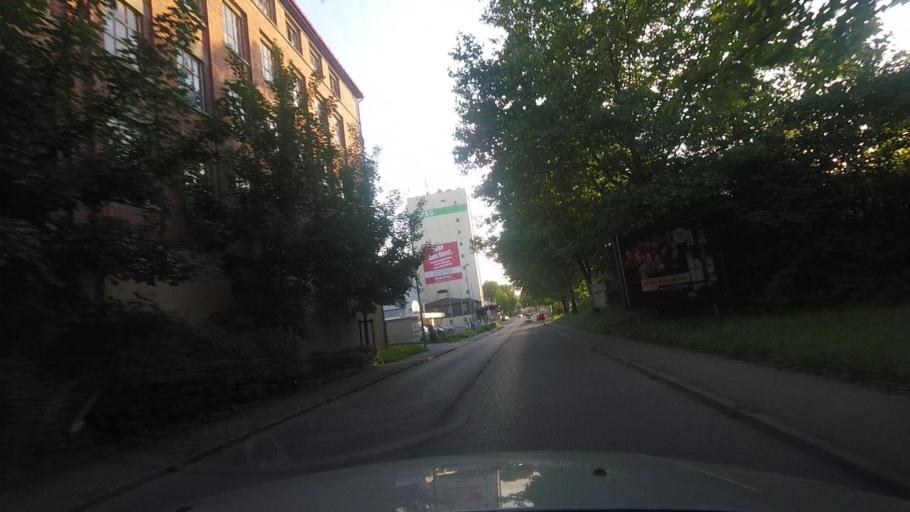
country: DE
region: Baden-Wuerttemberg
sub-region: Regierungsbezirk Stuttgart
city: Marbach am Neckar
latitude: 48.9449
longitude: 9.2728
